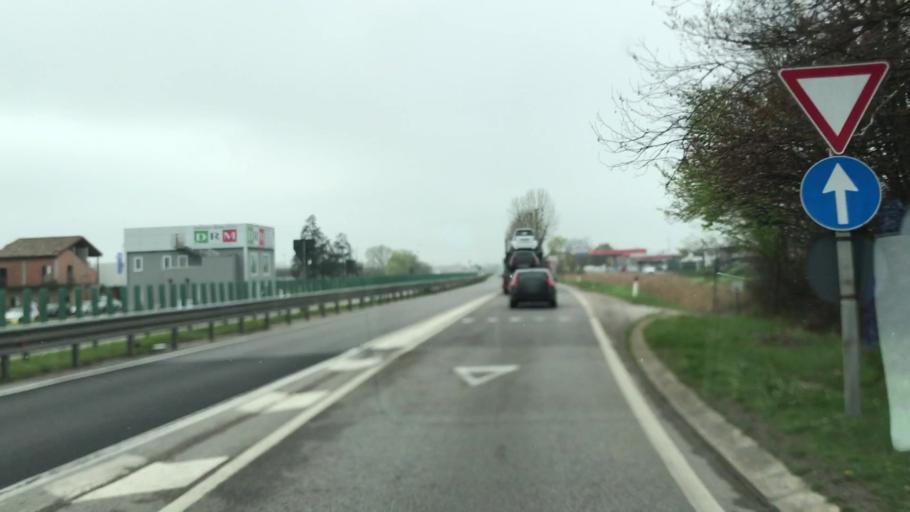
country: IT
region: Veneto
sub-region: Provincia di Rovigo
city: Grignano Polesine
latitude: 45.0379
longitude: 11.7808
